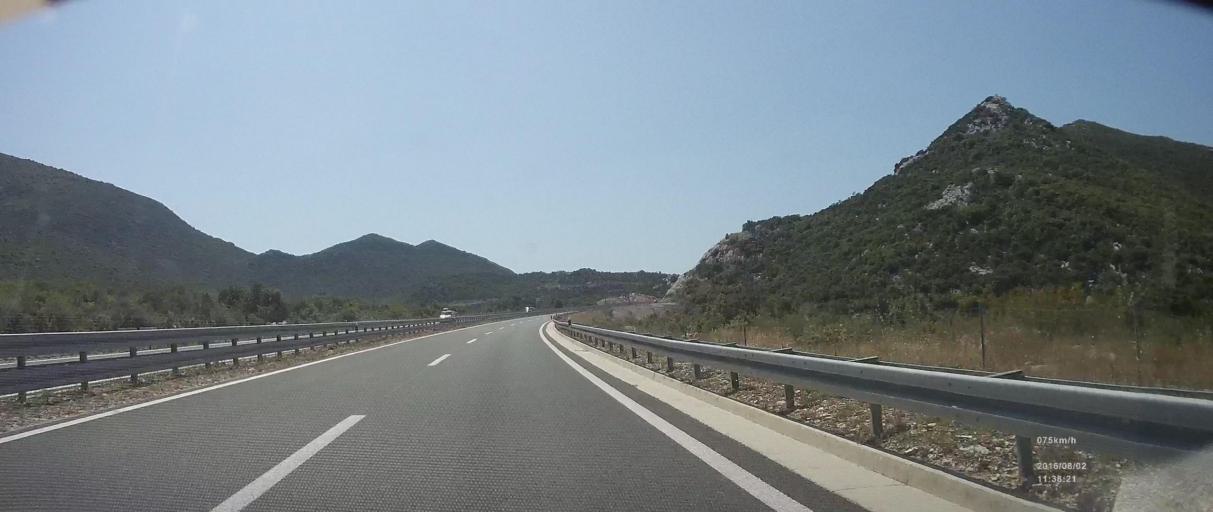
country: HR
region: Dubrovacko-Neretvanska
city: Komin
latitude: 43.0970
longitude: 17.4903
